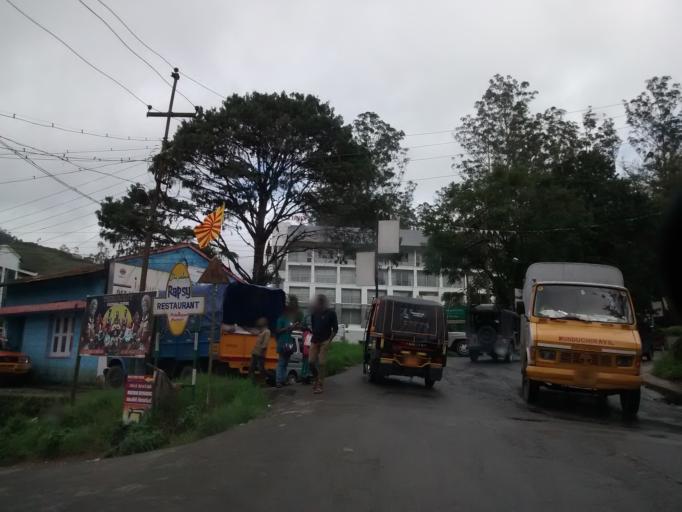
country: IN
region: Kerala
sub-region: Idukki
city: Munnar
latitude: 10.0872
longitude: 77.0614
